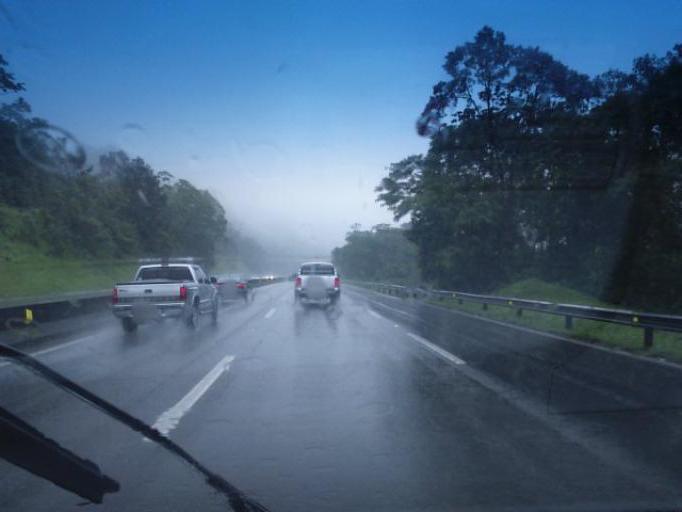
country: BR
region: Parana
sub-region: Guaratuba
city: Guaratuba
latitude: -25.8795
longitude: -48.9342
